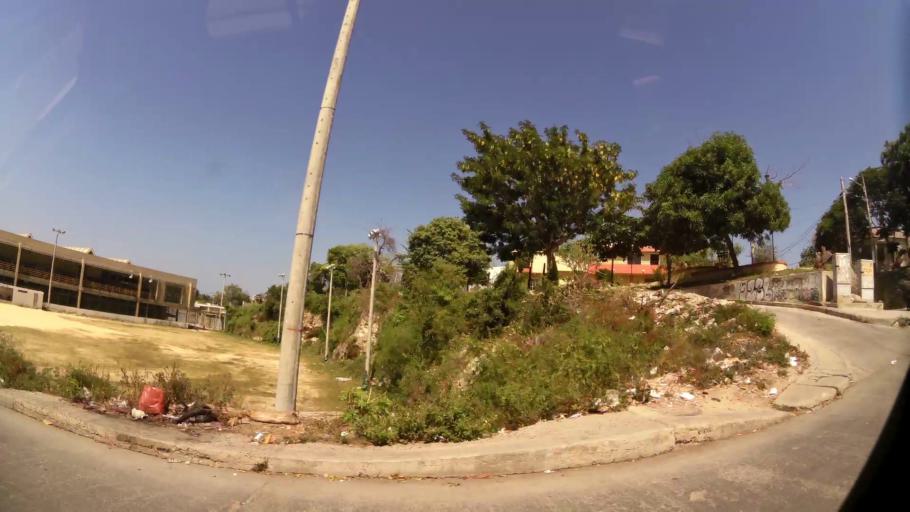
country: CO
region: Bolivar
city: Cartagena
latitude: 10.4353
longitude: -75.5269
